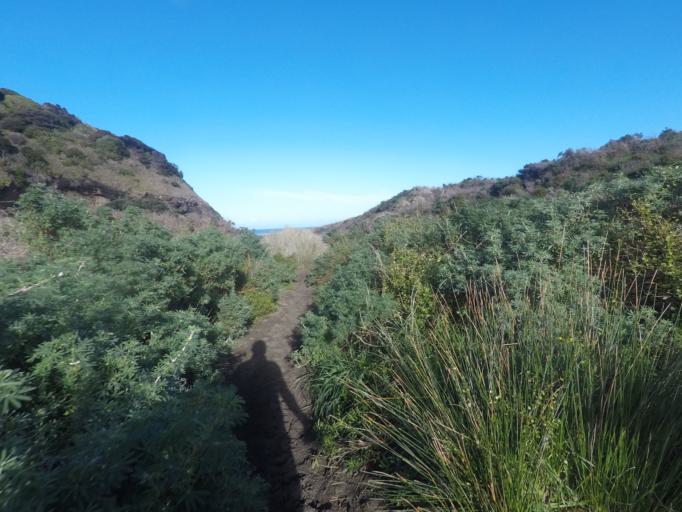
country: NZ
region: Auckland
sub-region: Auckland
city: Muriwai Beach
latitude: -36.9902
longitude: 174.4759
